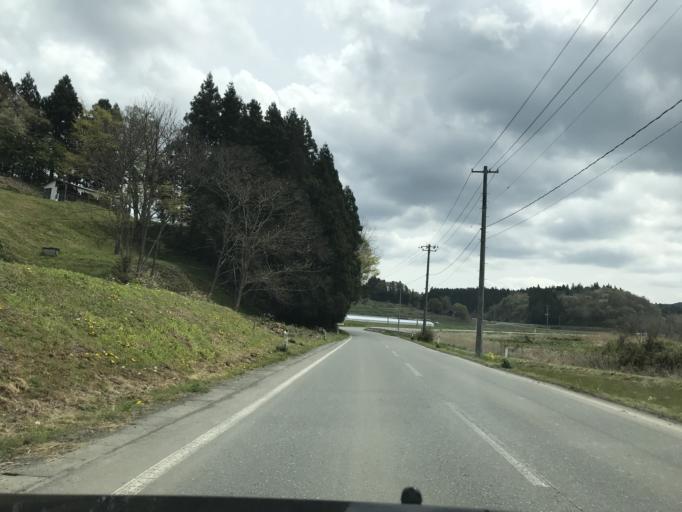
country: JP
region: Iwate
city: Ichinoseki
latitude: 38.8497
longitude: 141.3380
